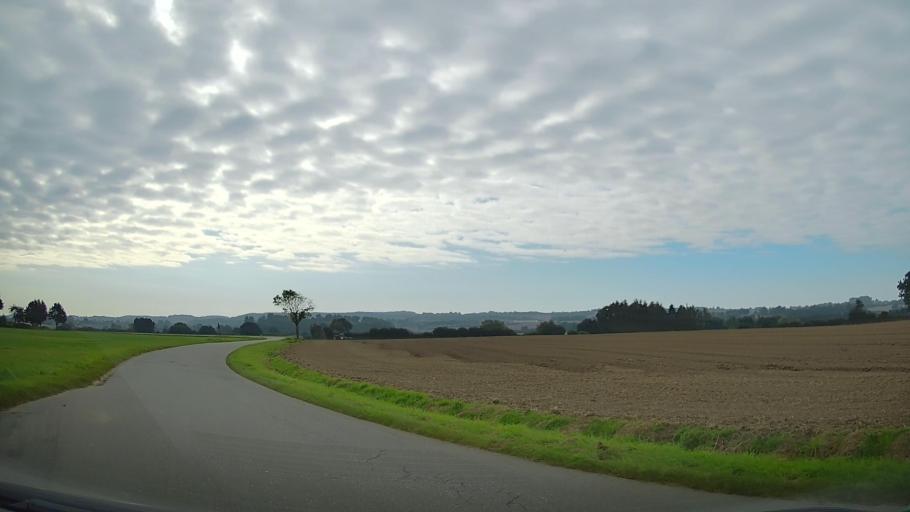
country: DE
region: Schleswig-Holstein
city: Panker
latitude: 54.3600
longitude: 10.5540
